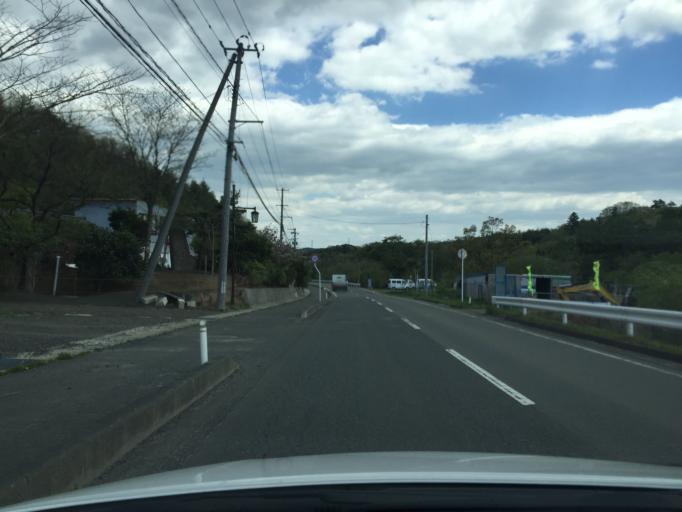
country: JP
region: Fukushima
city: Yanagawamachi-saiwaicho
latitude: 37.6824
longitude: 140.7386
